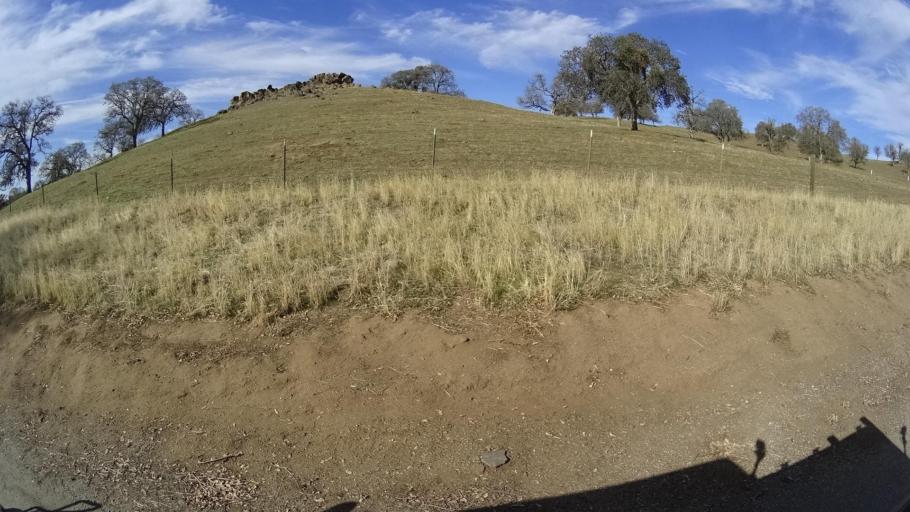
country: US
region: California
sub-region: Kern County
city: Oildale
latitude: 35.6003
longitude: -118.8252
